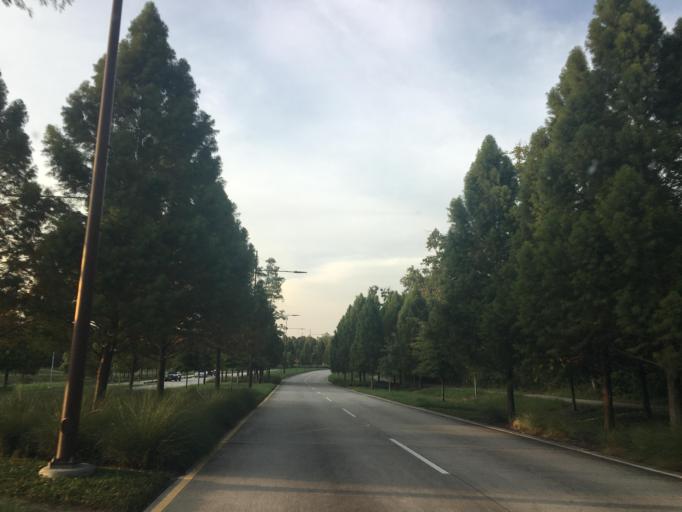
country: US
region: Texas
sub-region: Harris County
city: Spring
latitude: 30.1001
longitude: -95.4386
